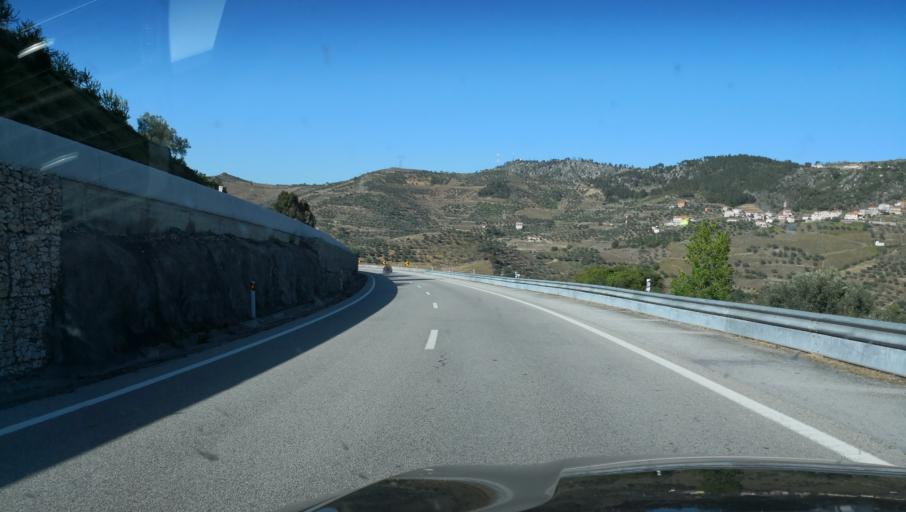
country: PT
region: Viseu
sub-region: Lamego
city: Lamego
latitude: 41.1012
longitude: -7.7760
